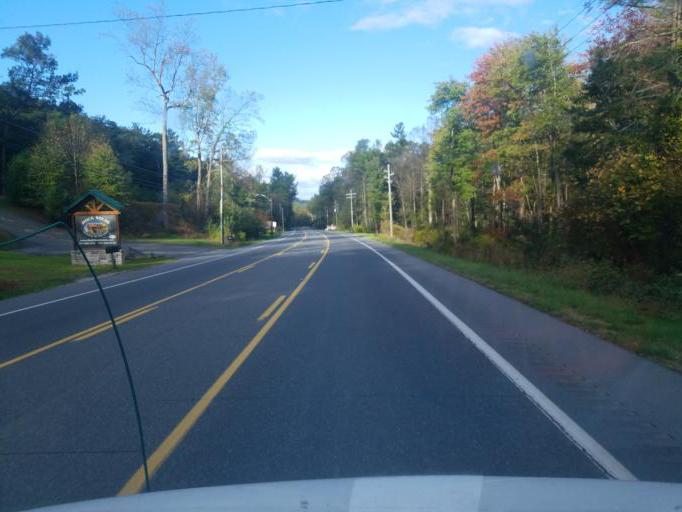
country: US
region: Pennsylvania
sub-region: Franklin County
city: Fayetteville
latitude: 39.8996
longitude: -77.4427
